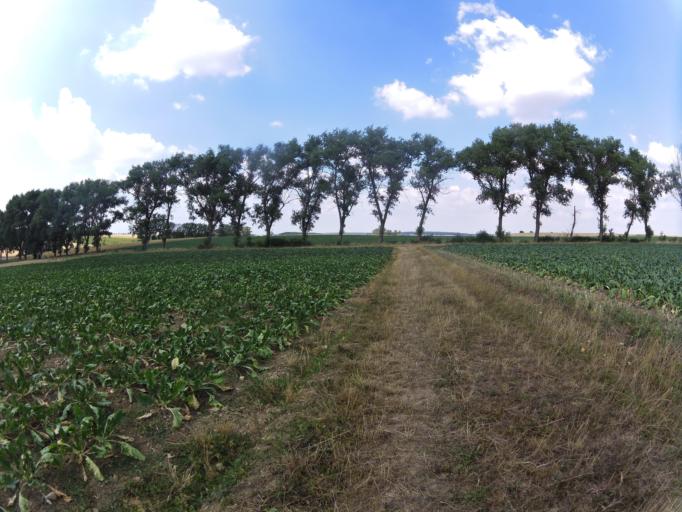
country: DE
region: Bavaria
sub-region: Regierungsbezirk Unterfranken
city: Ochsenfurt
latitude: 49.6425
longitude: 10.0624
